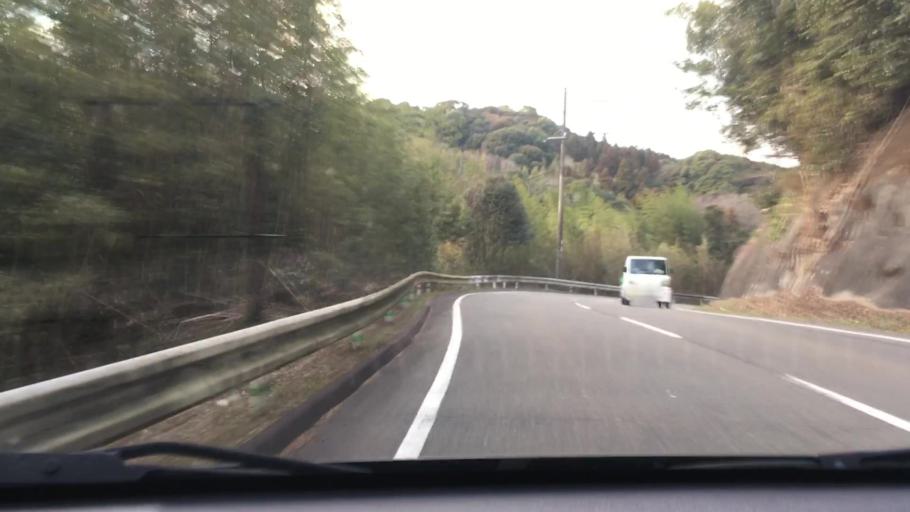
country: JP
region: Oita
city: Hiji
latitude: 33.4163
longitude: 131.4193
